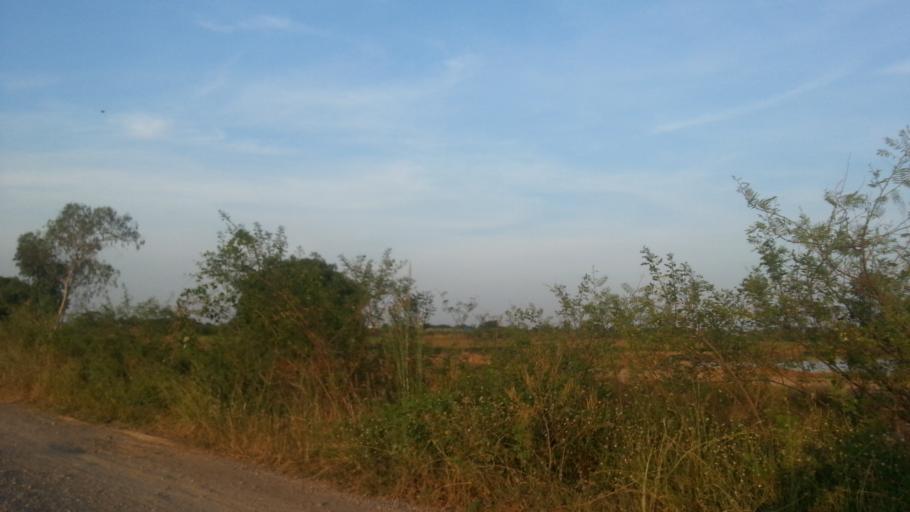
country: TH
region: Pathum Thani
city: Ban Lam Luk Ka
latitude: 14.0351
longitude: 100.8566
